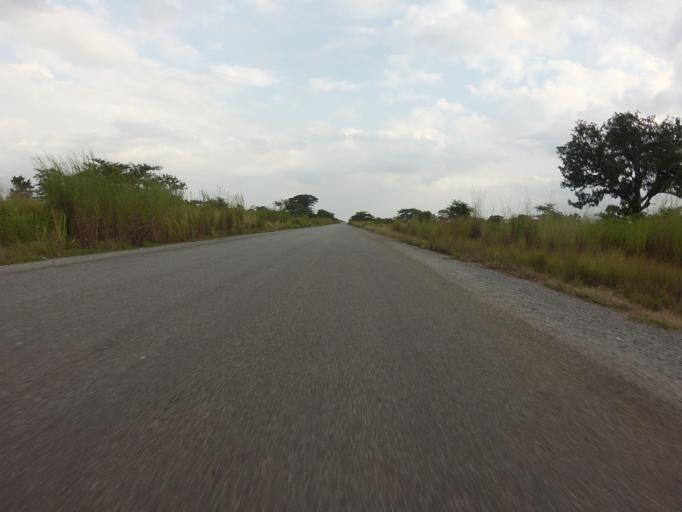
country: GH
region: Volta
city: Ho
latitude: 6.4182
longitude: 0.5202
